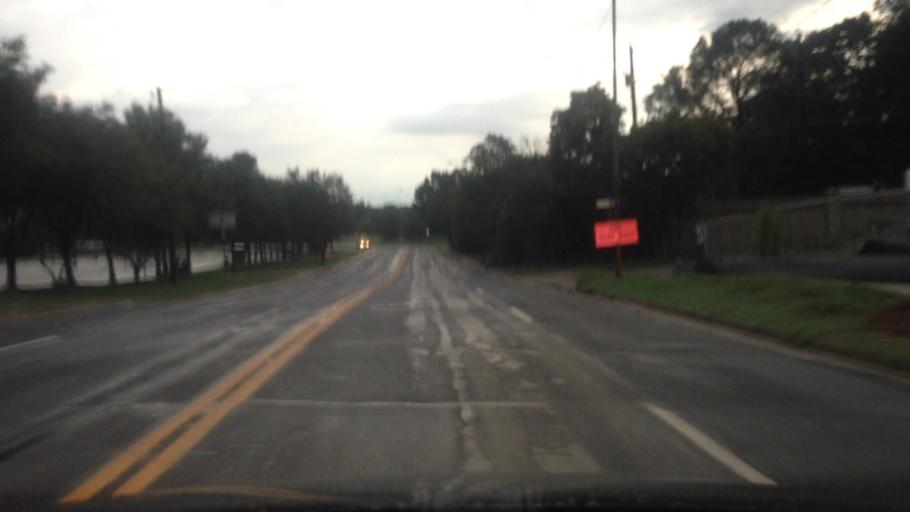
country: US
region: Texas
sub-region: Tarrant County
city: Arlington
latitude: 32.7554
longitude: -97.0887
